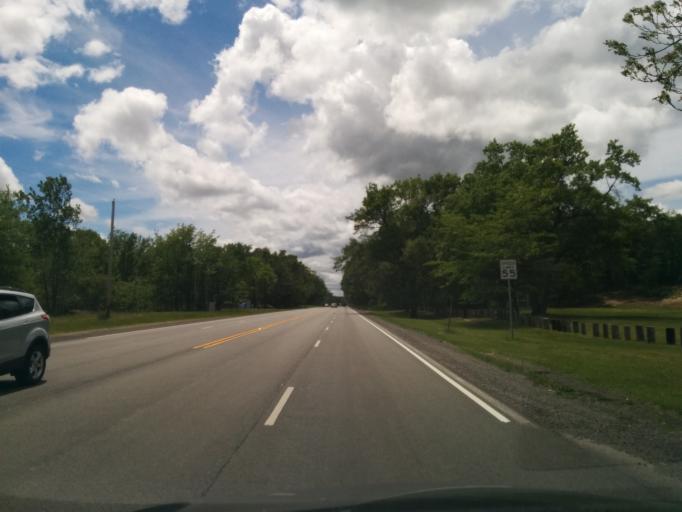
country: US
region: Indiana
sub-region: LaPorte County
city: Michigan City
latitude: 41.6786
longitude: -86.9620
